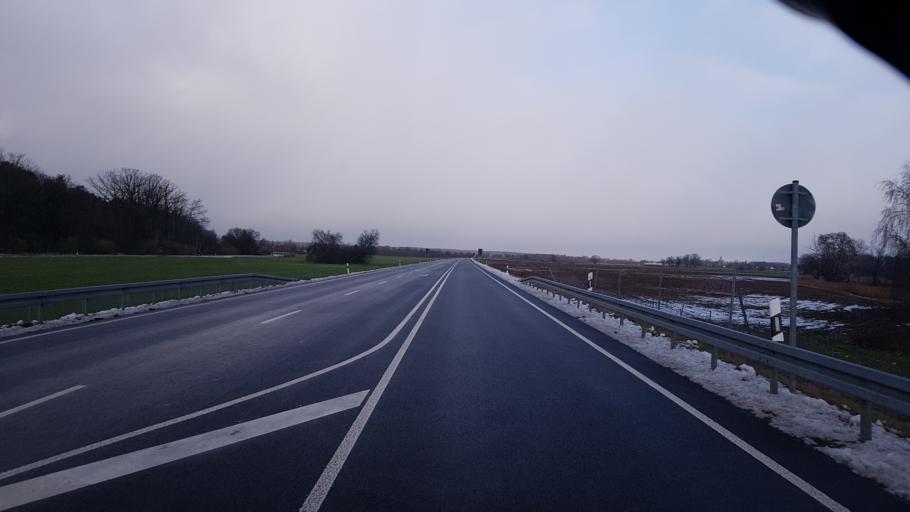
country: DE
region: Brandenburg
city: Schenkendobern
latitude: 51.8686
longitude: 14.6208
